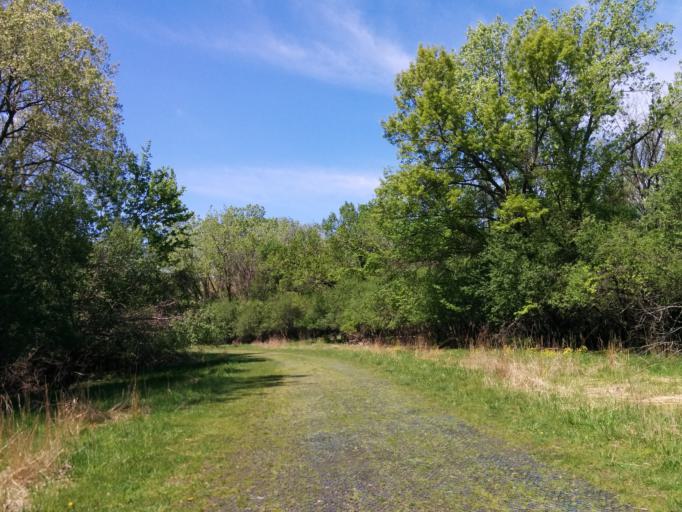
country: US
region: Illinois
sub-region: Cook County
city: Norridge
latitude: 41.9737
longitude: -87.8500
